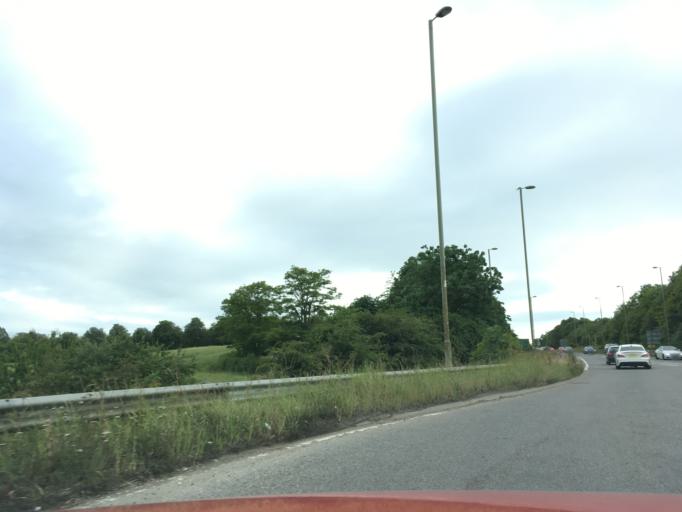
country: GB
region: England
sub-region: Oxfordshire
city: Faringdon
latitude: 51.6493
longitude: -1.5746
